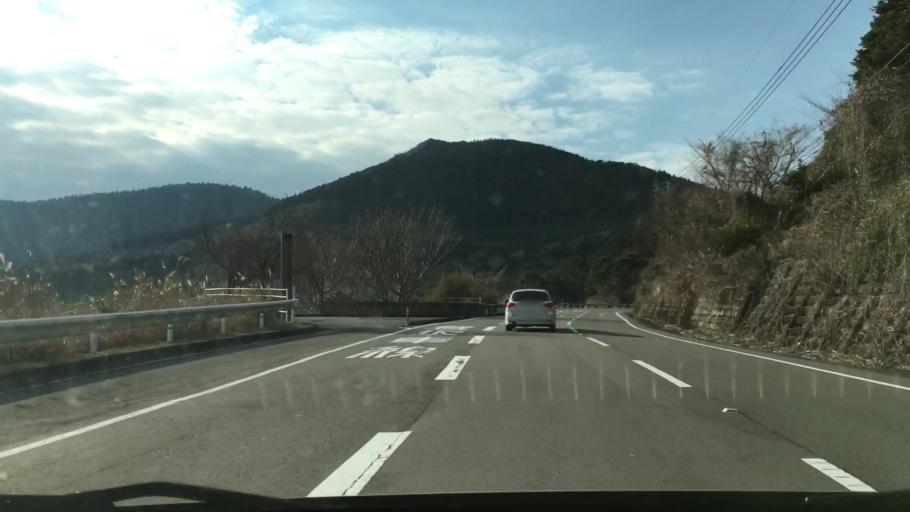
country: JP
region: Miyazaki
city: Miyazaki-shi
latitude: 31.7800
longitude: 131.3265
